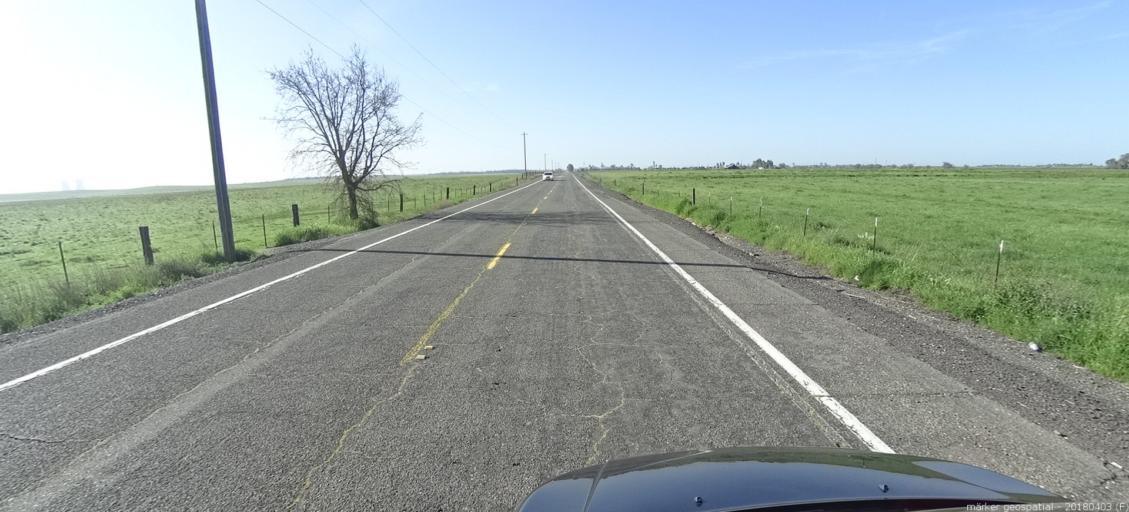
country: US
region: California
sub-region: Sacramento County
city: Clay
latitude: 38.3826
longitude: -121.1685
